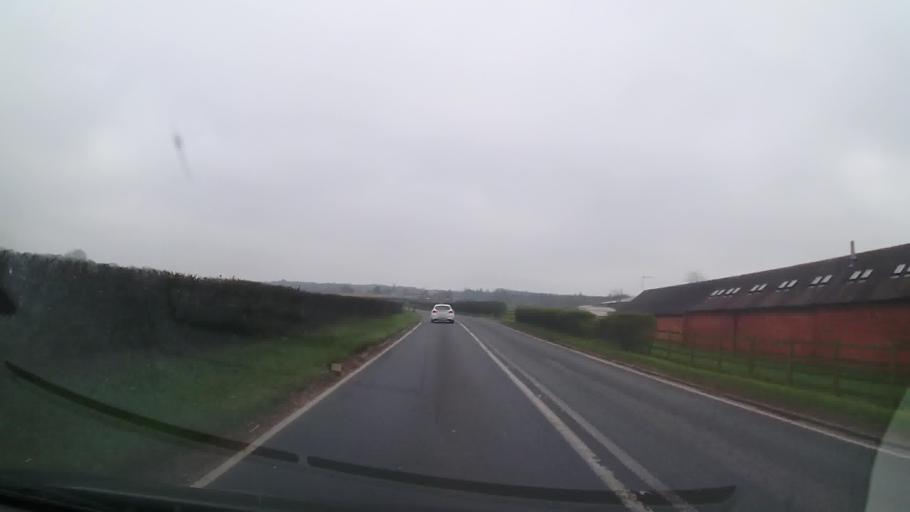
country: GB
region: England
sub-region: Shropshire
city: Market Drayton
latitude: 52.9207
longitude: -2.4034
